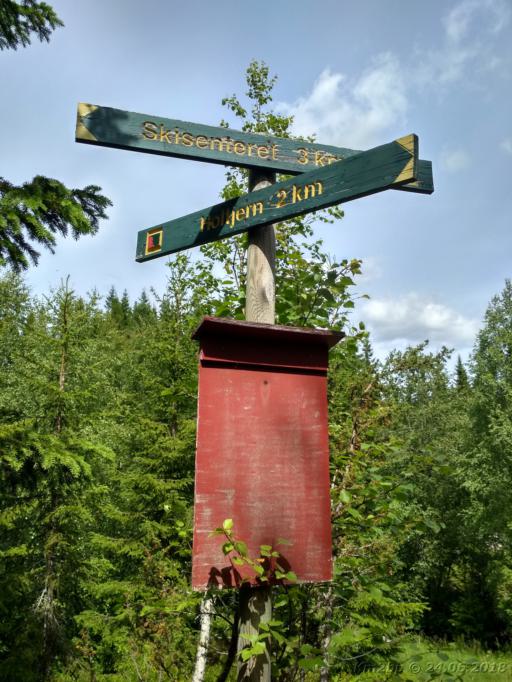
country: NO
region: Akershus
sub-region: Hurdal
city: Hurdal
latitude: 60.4823
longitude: 11.0833
